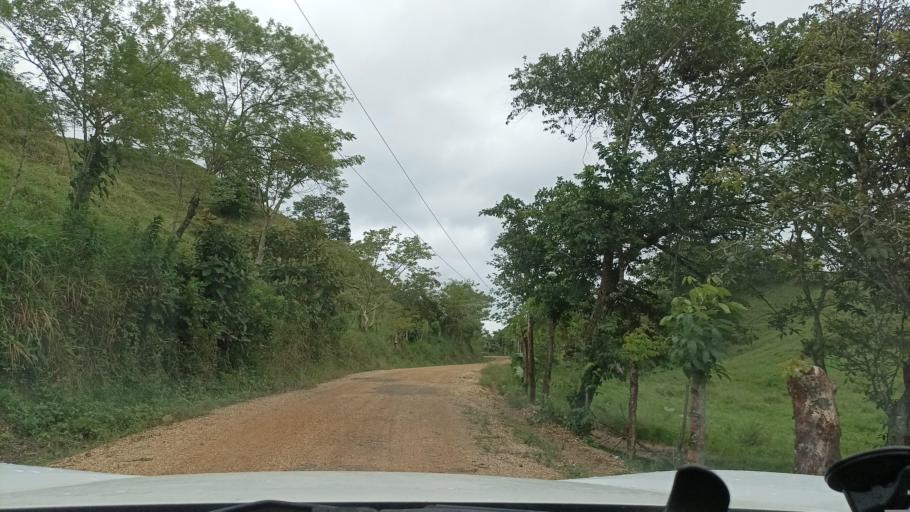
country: MX
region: Veracruz
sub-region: Moloacan
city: Cuichapa
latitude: 17.7892
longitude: -94.3853
